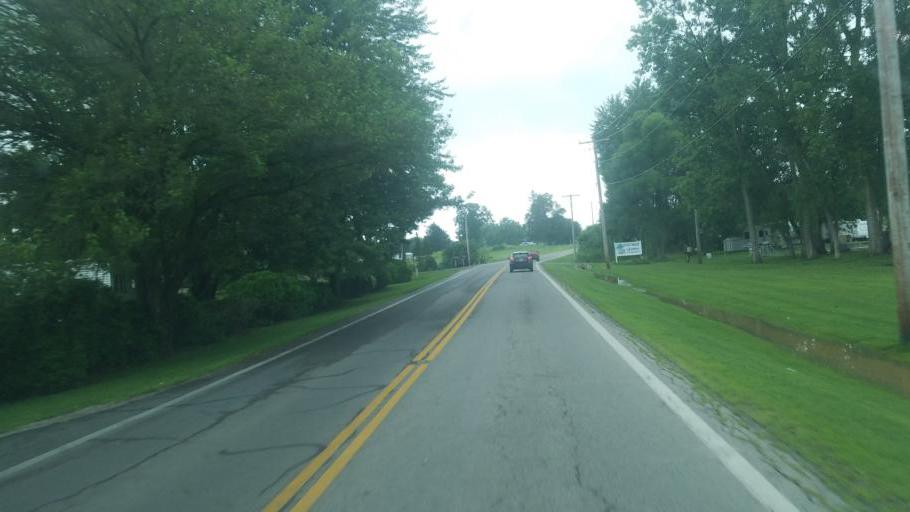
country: US
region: Ohio
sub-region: Logan County
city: Russells Point
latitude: 40.5290
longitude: -83.8476
